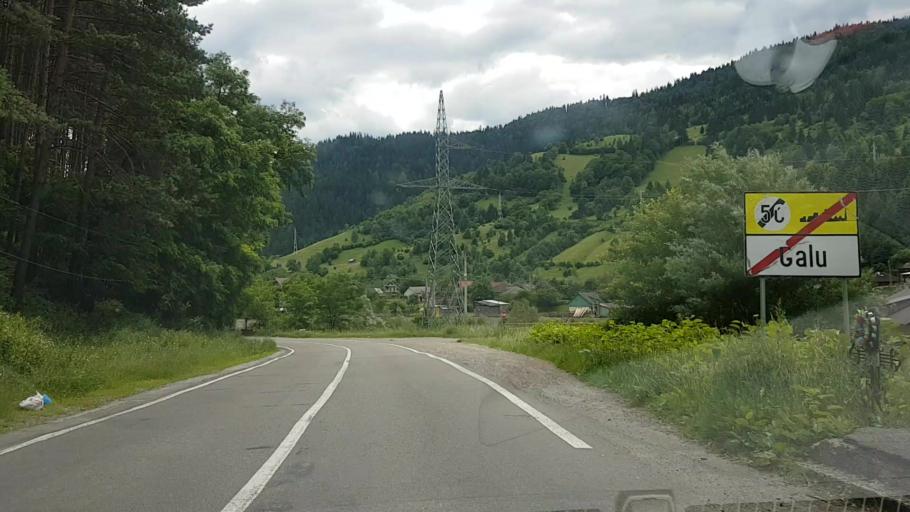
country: RO
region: Neamt
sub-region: Comuna Poiana Teiului
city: Poiana Teiului
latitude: 47.1233
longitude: 25.9075
